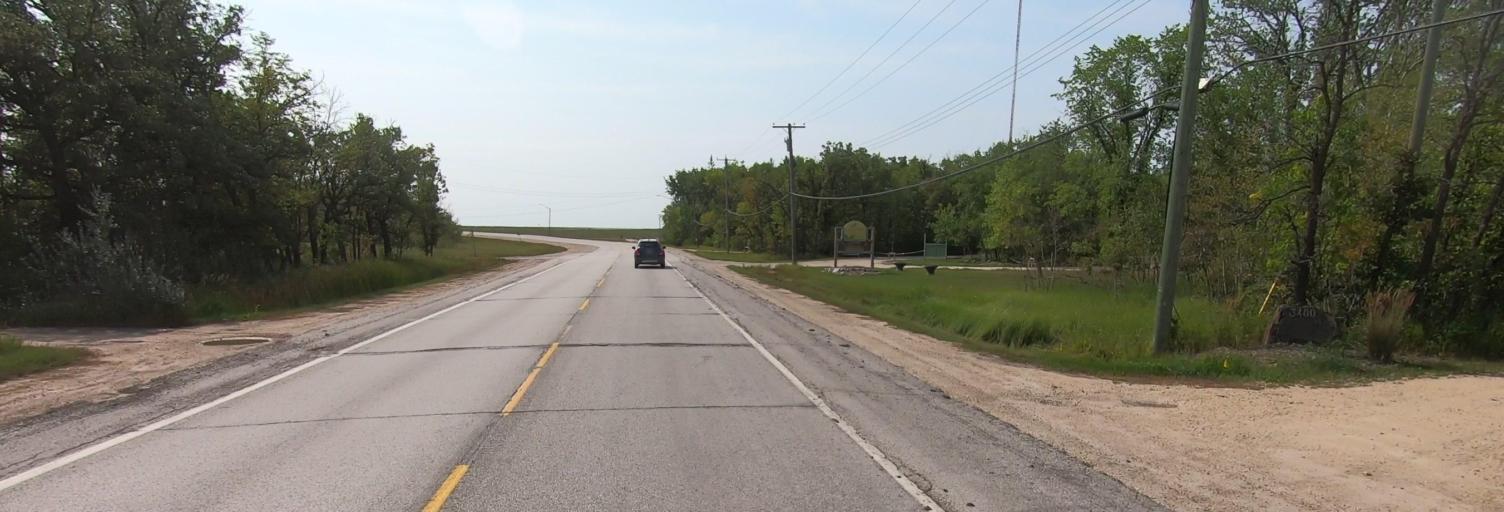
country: CA
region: Manitoba
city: Winnipeg
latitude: 49.7612
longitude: -97.1279
